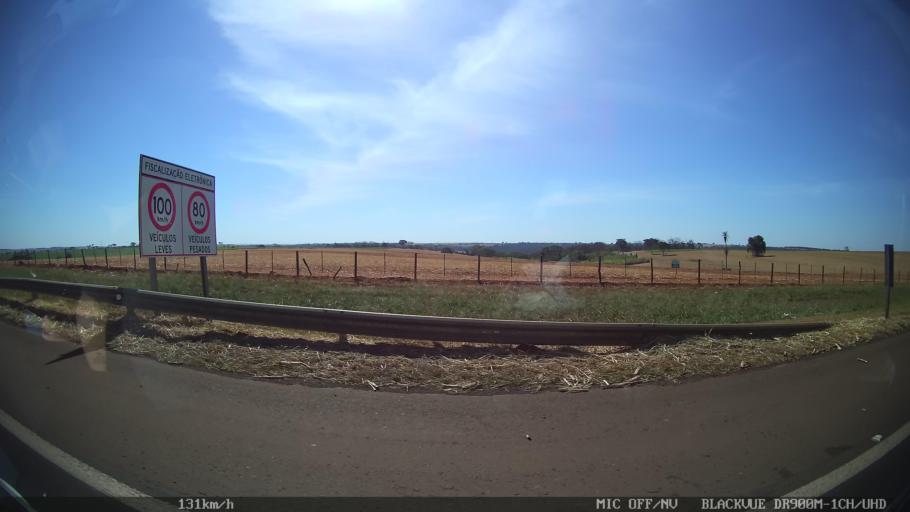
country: BR
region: Sao Paulo
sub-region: Olimpia
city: Olimpia
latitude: -20.6254
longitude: -48.7852
